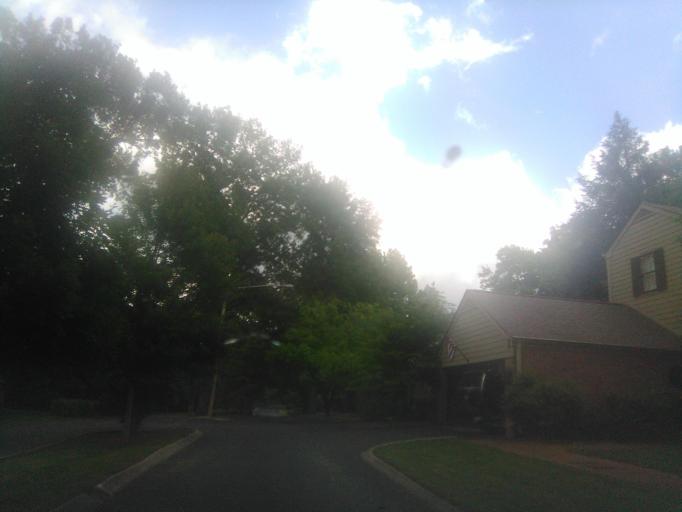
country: US
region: Tennessee
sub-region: Davidson County
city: Belle Meade
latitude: 36.1137
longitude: -86.8359
